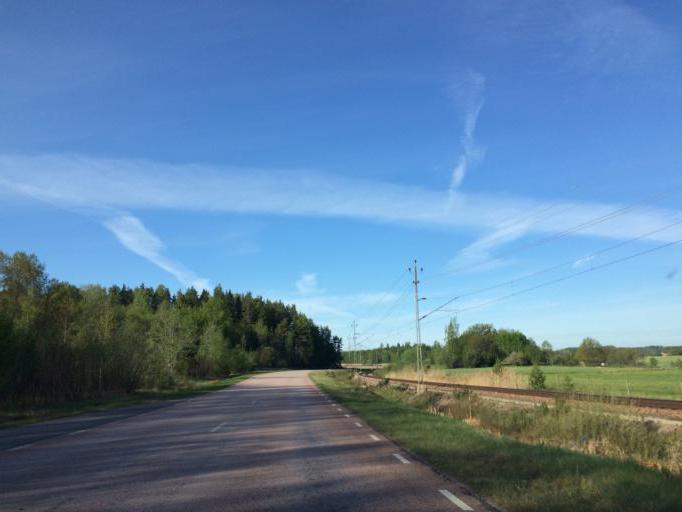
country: SE
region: Soedermanland
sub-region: Eskilstuna Kommun
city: Kvicksund
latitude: 59.4127
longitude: 16.2735
